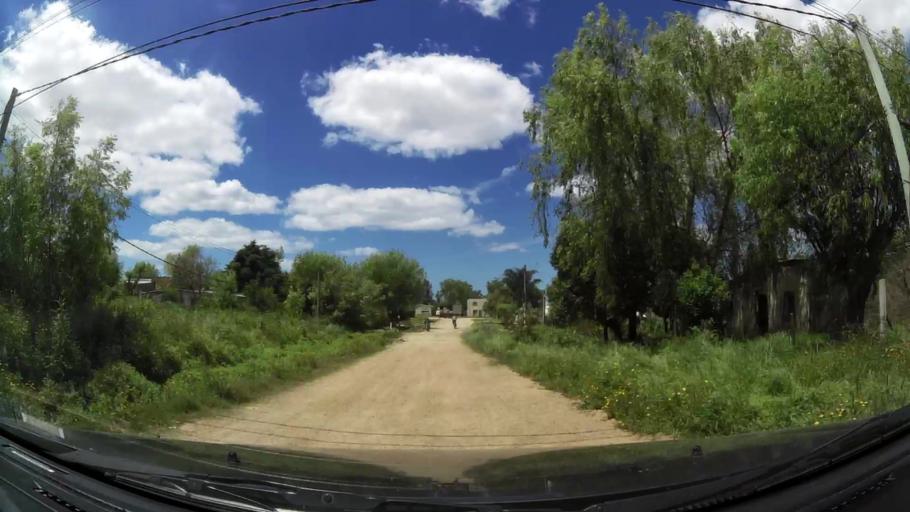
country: UY
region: Canelones
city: Colonia Nicolich
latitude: -34.8182
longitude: -55.9994
